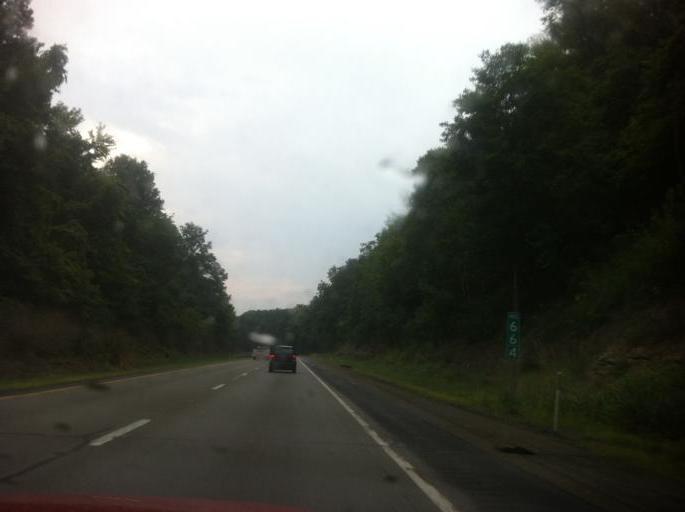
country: US
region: Pennsylvania
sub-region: Clarion County
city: Clarion
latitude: 41.1814
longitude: -79.3160
